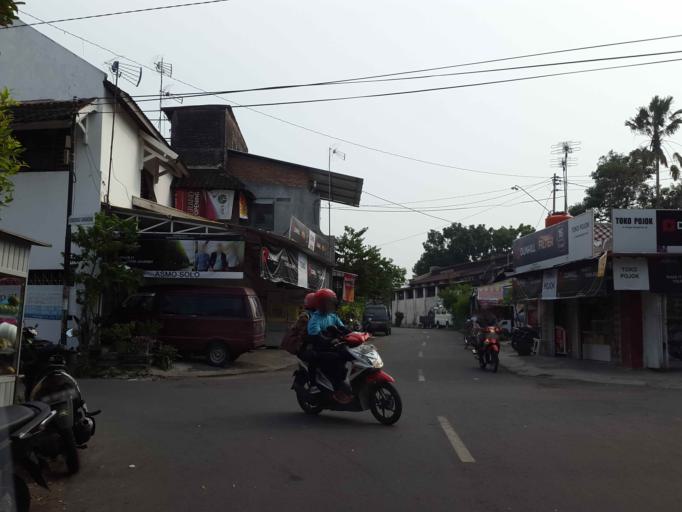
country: ID
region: Central Java
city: Surakarta
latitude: -7.5749
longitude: 110.8372
